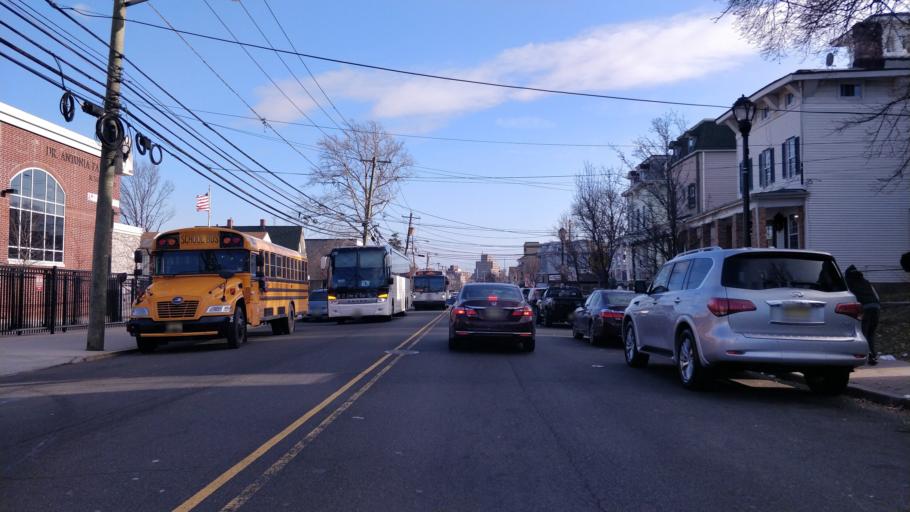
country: US
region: New Jersey
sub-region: Union County
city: Elizabeth
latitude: 40.6731
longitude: -74.2233
